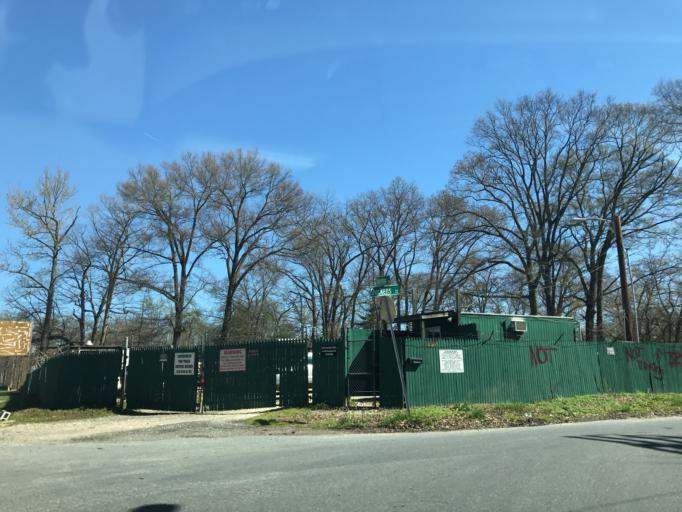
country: US
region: Maryland
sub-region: Anne Arundel County
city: Odenton
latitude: 39.0899
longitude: -76.7133
